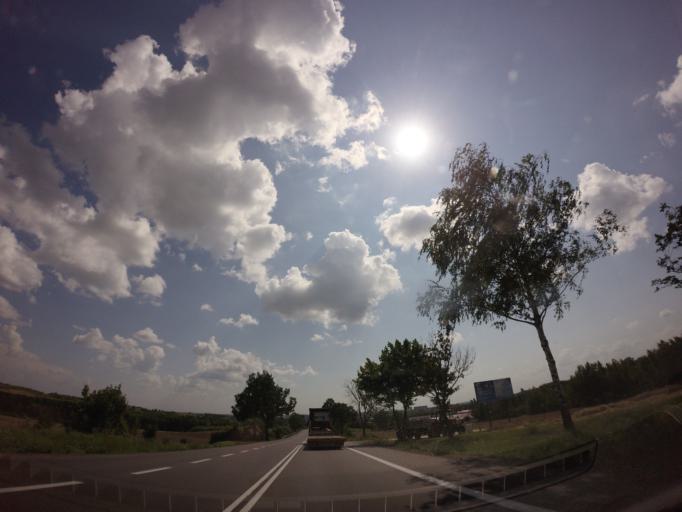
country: PL
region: Podlasie
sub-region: Powiat lomzynski
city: Piatnica
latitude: 53.2073
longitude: 22.1026
